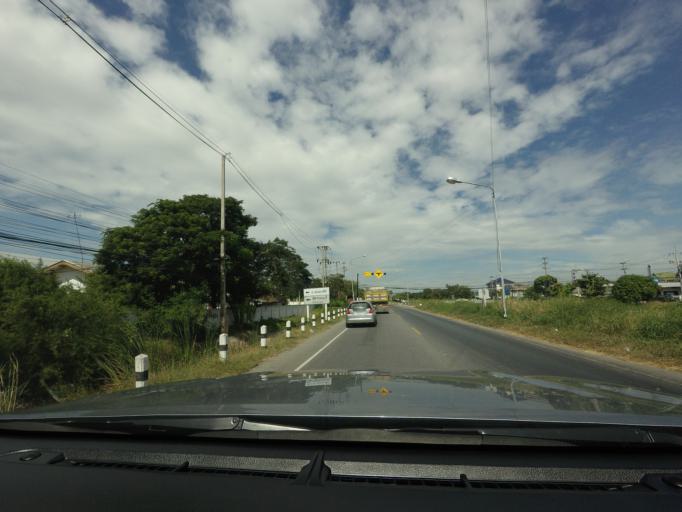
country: TH
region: Suphan Buri
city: Suphan Buri
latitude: 14.4744
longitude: 100.0914
